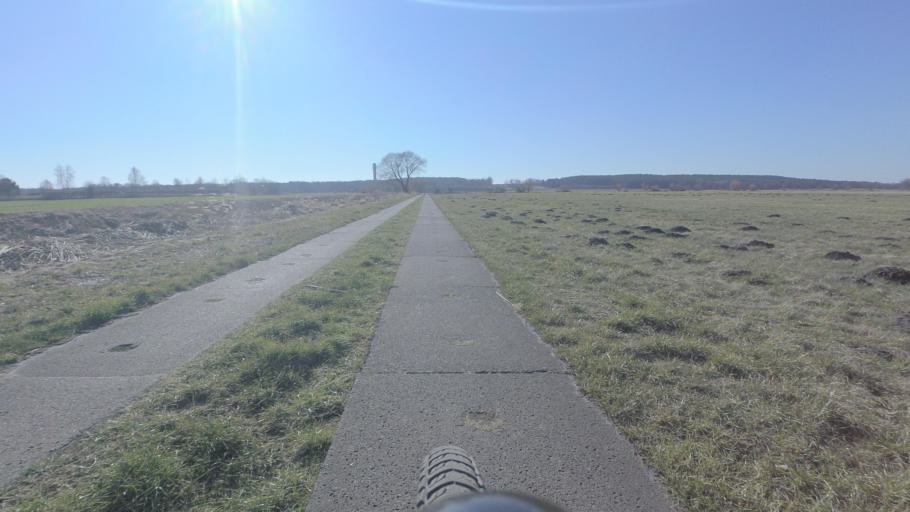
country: DE
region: Brandenburg
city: Rangsdorf
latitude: 52.2612
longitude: 13.4158
